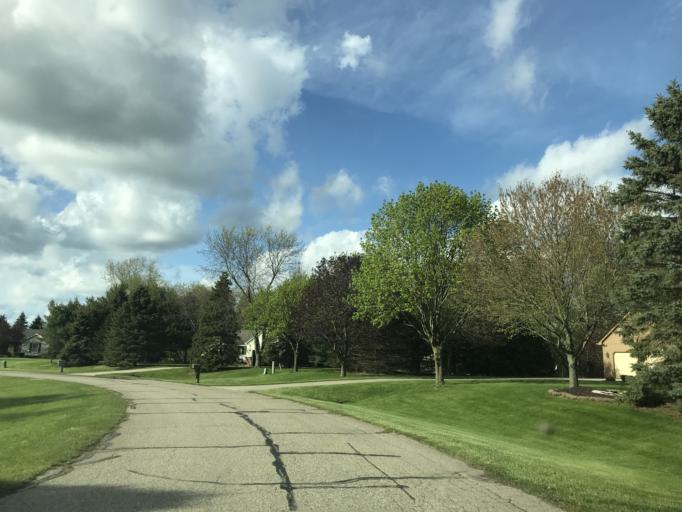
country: US
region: Michigan
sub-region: Livingston County
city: Brighton
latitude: 42.5430
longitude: -83.7143
